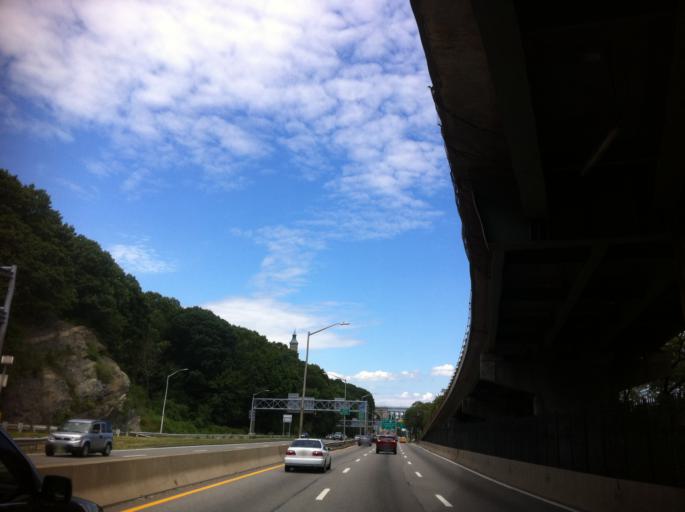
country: US
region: New York
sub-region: New York County
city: Inwood
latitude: 40.8314
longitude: -73.9351
